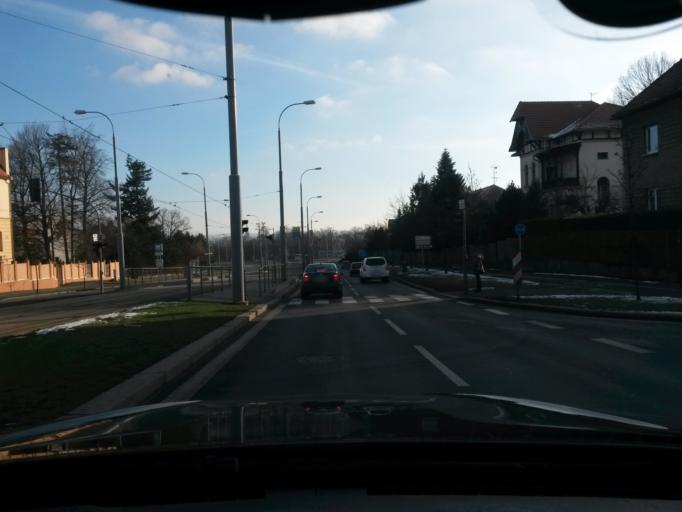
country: CZ
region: Plzensky
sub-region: Okres Plzen-Mesto
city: Pilsen
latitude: 49.7643
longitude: 13.3644
